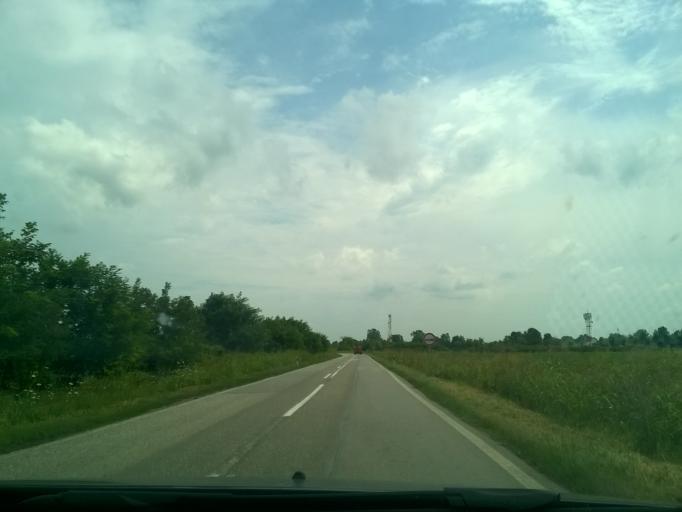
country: RS
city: Hajducica
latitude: 45.2585
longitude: 20.9608
